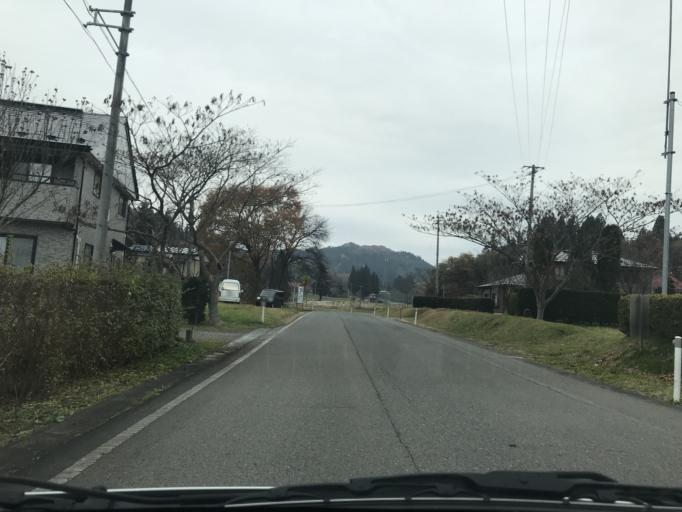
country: JP
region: Iwate
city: Kitakami
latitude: 39.2746
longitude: 141.1756
